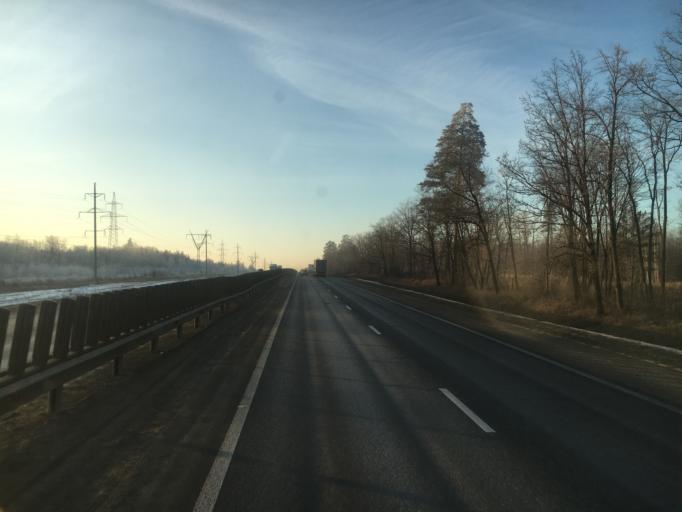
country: RU
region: Samara
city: Pribrezhnyy
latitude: 53.5155
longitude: 49.8726
